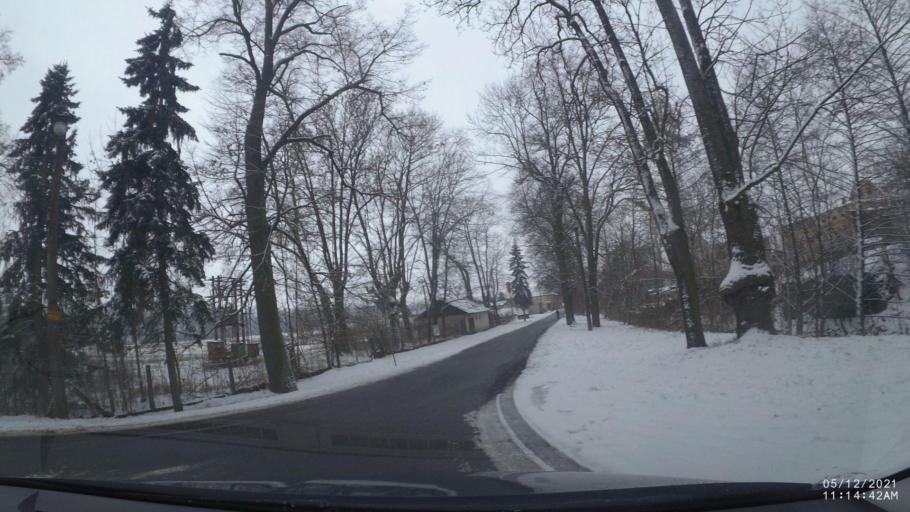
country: CZ
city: Solnice
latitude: 50.1875
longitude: 16.2139
